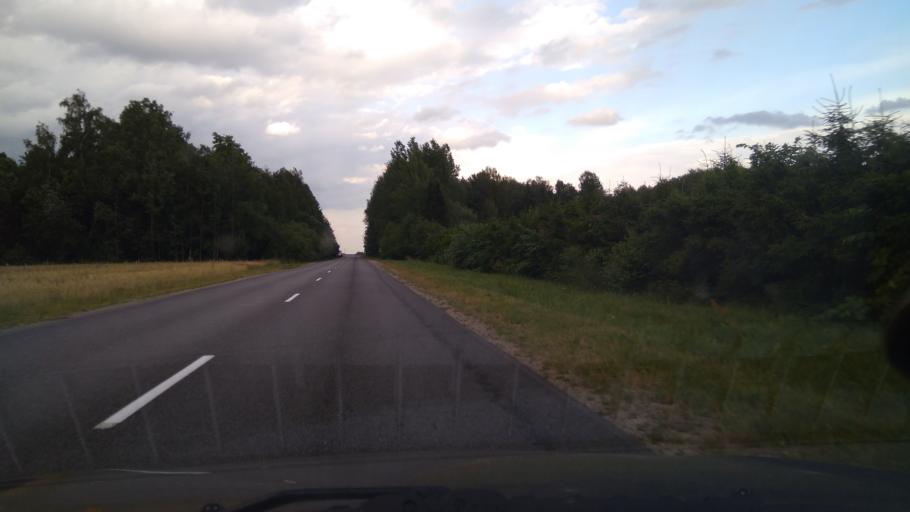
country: BY
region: Minsk
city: Il'ya
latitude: 54.4113
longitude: 27.2574
